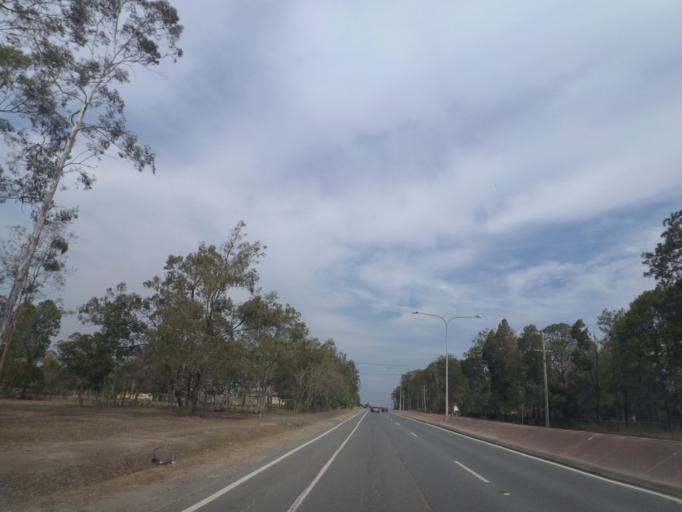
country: AU
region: Queensland
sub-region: Brisbane
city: Sunnybank
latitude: -27.5967
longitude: 153.0228
